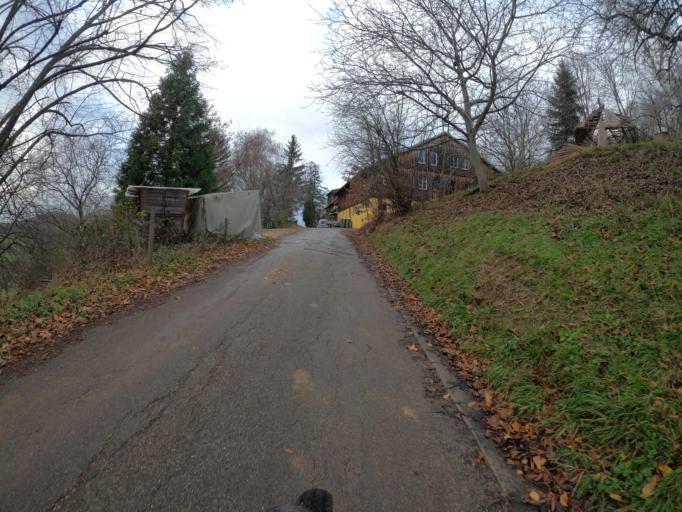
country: DE
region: Baden-Wuerttemberg
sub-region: Regierungsbezirk Stuttgart
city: Waldstetten
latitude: 48.7565
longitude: 9.8376
